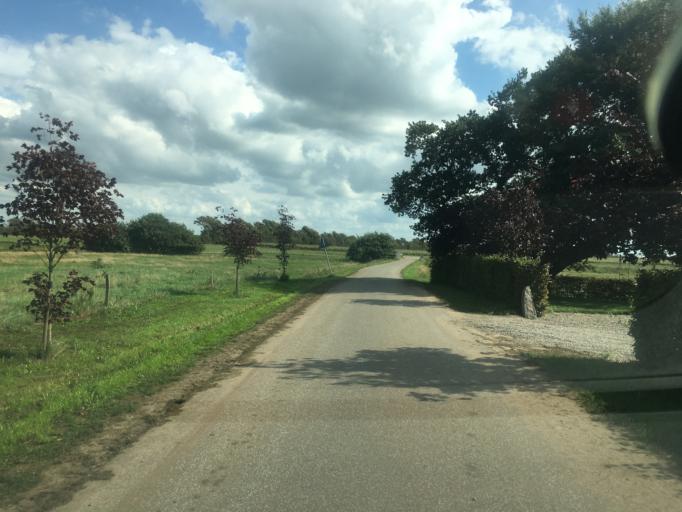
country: DK
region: South Denmark
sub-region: Tonder Kommune
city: Logumkloster
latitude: 54.9982
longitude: 9.0120
